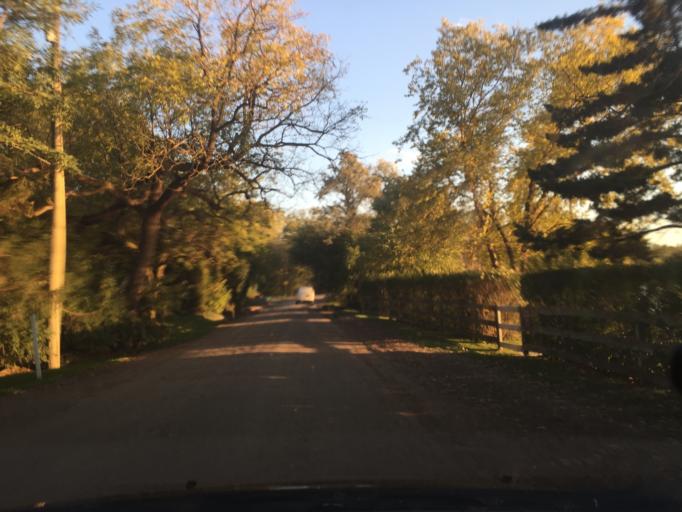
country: US
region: Michigan
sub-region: Oakland County
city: Franklin
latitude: 42.5556
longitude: -83.2946
